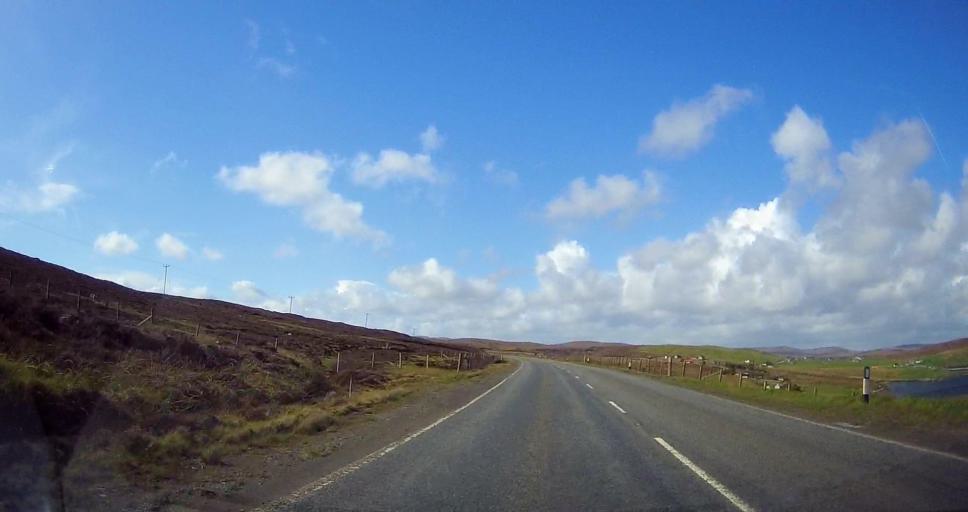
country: GB
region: Scotland
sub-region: Shetland Islands
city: Lerwick
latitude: 60.2241
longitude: -1.2347
